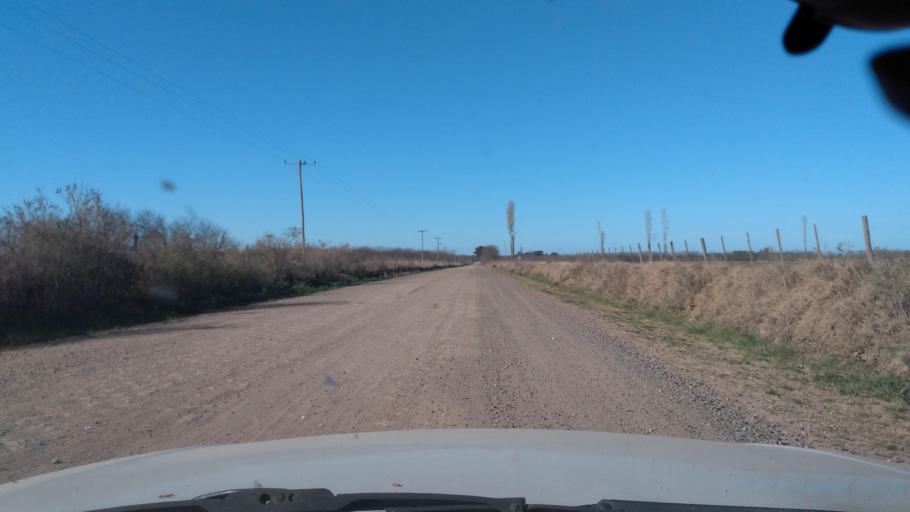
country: AR
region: Buenos Aires
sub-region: Partido de Mercedes
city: Mercedes
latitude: -34.6169
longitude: -59.3353
